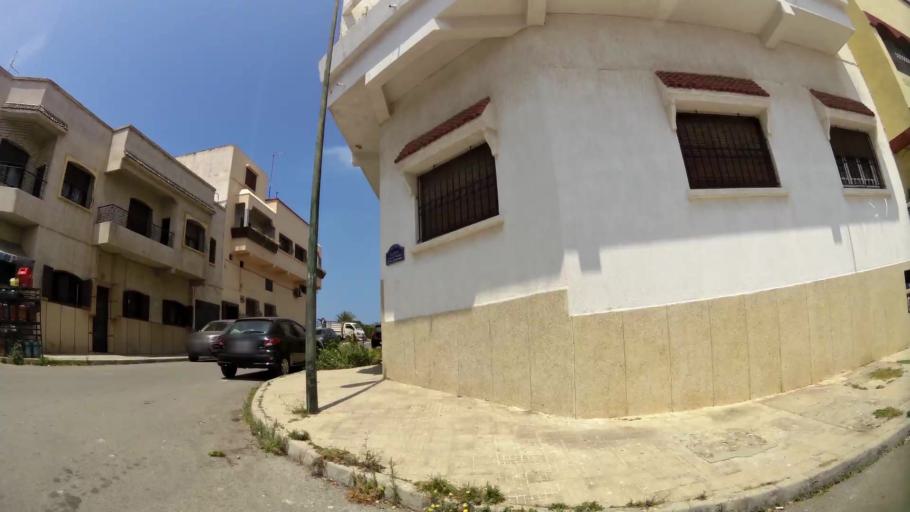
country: MA
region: Rabat-Sale-Zemmour-Zaer
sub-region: Skhirate-Temara
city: Temara
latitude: 33.9776
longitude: -6.8909
